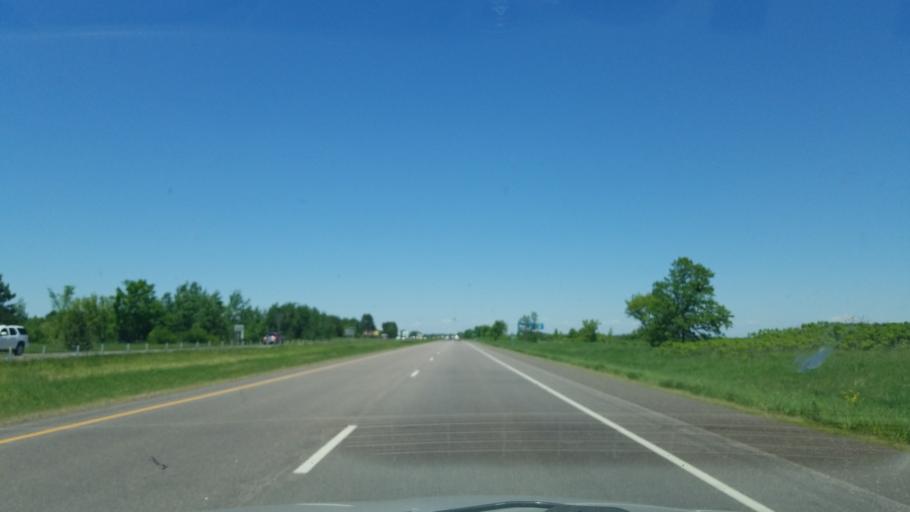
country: US
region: Minnesota
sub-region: Pine County
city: Rock Creek
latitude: 45.7268
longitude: -92.9917
